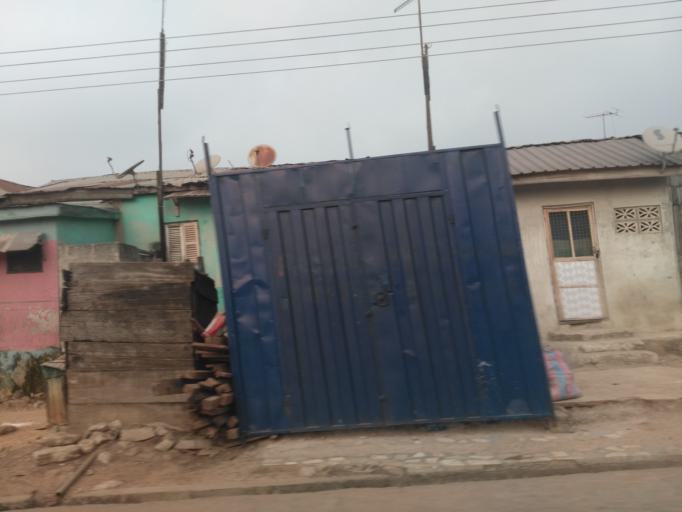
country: GH
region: Ashanti
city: Kumasi
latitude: 6.6842
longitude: -1.5904
